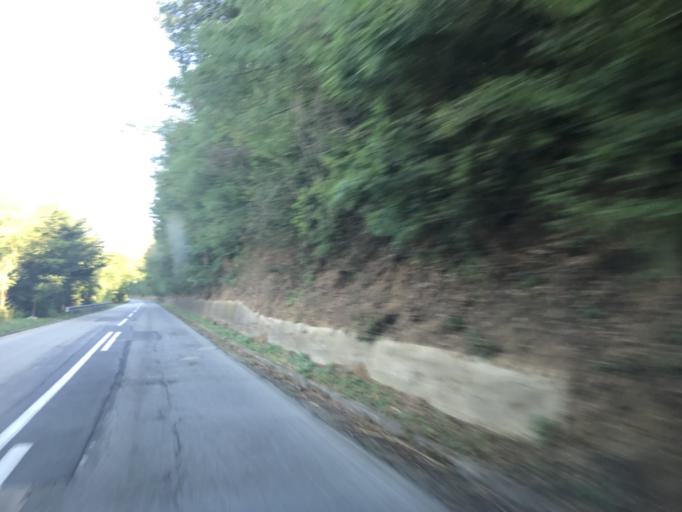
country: RO
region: Caras-Severin
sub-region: Comuna Berzasca
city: Liubcova
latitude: 44.6458
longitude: 21.8711
